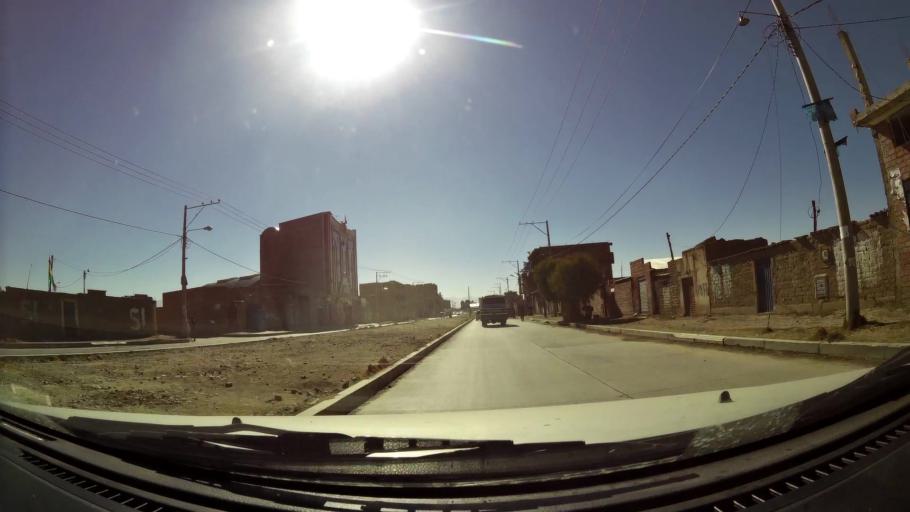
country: BO
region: La Paz
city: La Paz
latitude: -16.5368
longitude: -68.2223
